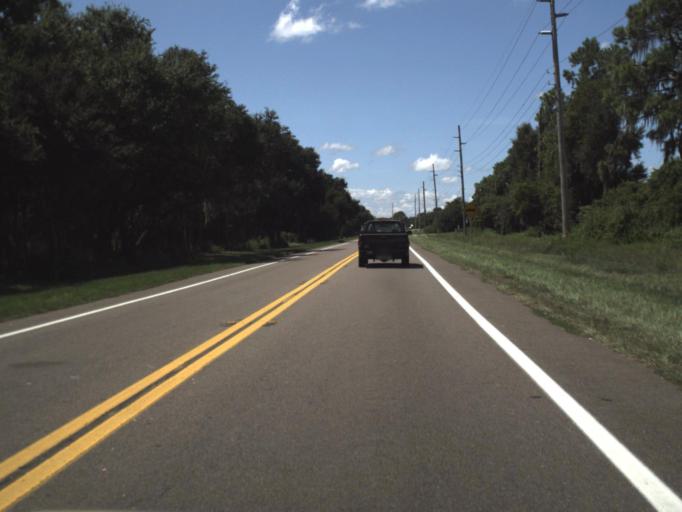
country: US
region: Florida
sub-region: Polk County
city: Lake Alfred
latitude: 28.0697
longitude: -81.6944
